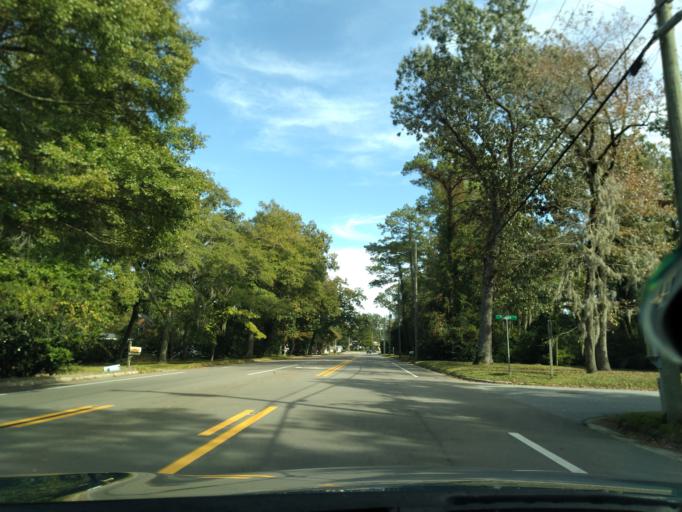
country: US
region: North Carolina
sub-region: Beaufort County
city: Washington
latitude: 35.5343
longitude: -77.0278
